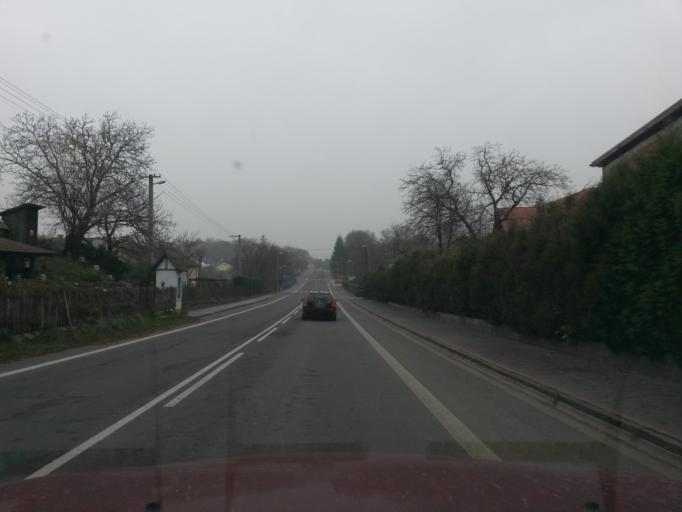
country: SK
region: Kosicky
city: Kosice
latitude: 48.8009
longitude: 21.3033
